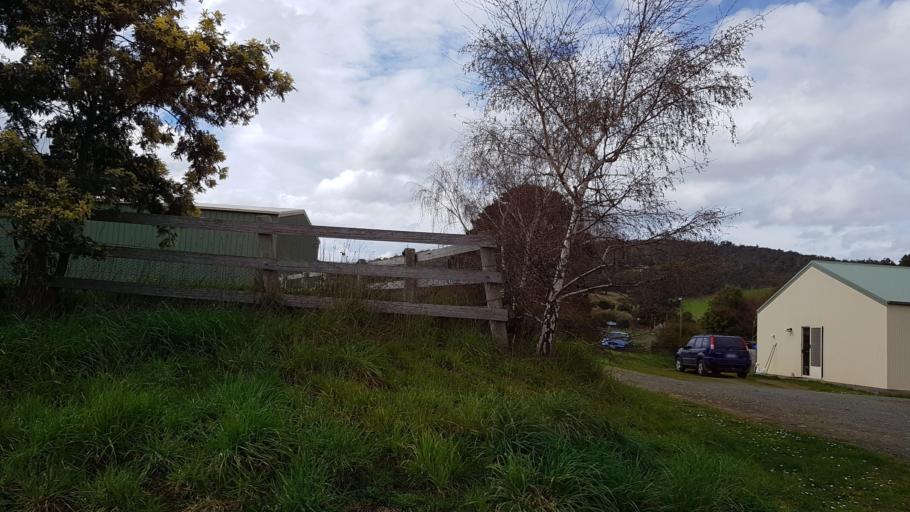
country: AU
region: Tasmania
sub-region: Huon Valley
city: Huonville
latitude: -42.9970
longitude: 147.0657
